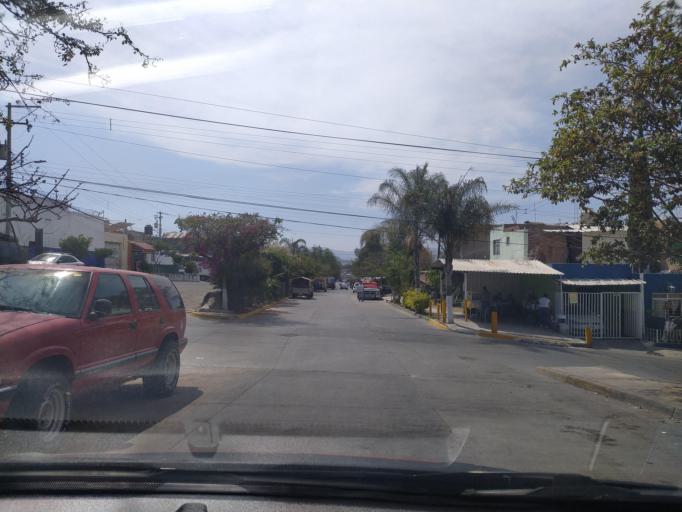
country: MX
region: Jalisco
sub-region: Tlajomulco de Zuniga
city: Altus Bosques
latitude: 20.6117
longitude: -103.3706
